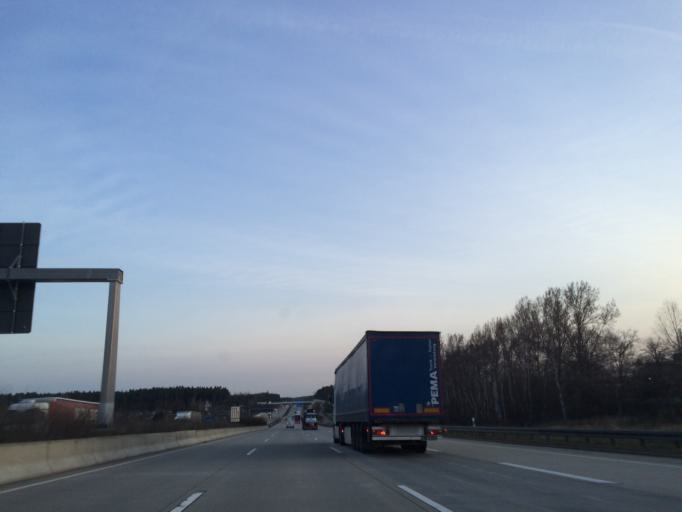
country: DE
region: Thuringia
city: Hermsdorf
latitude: 50.8942
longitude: 11.8445
